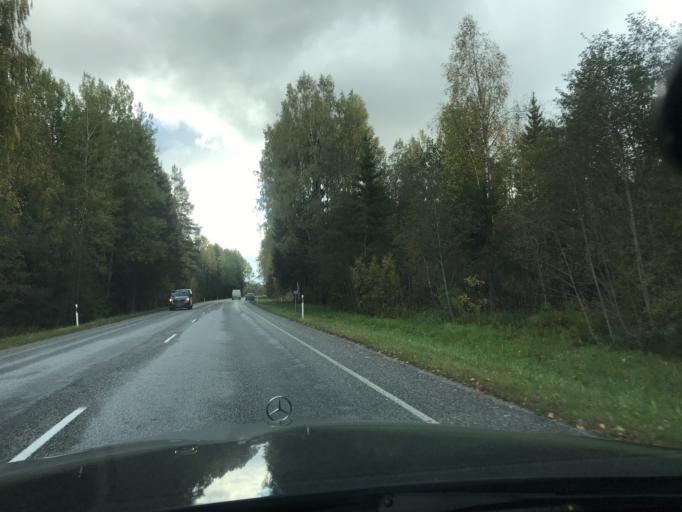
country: RU
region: Pskov
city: Pechory
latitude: 57.7236
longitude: 27.3145
